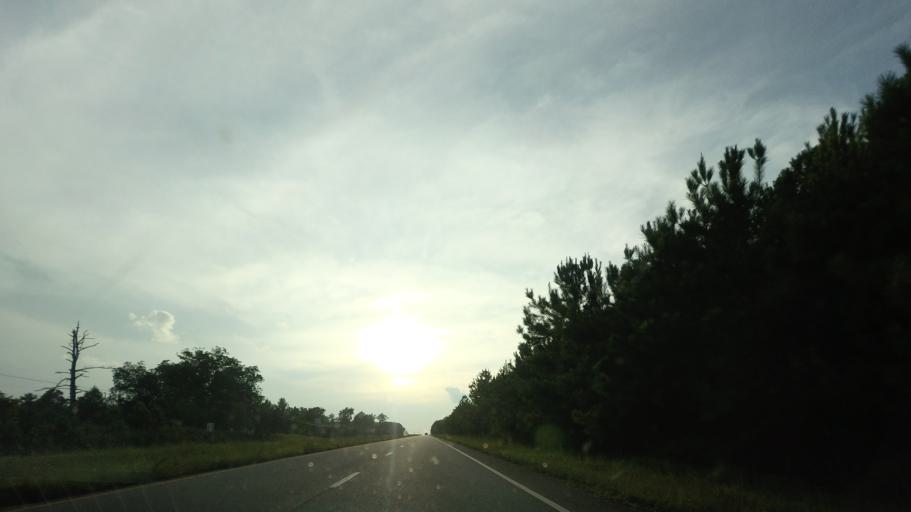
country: US
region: Georgia
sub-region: Wilkinson County
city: Gordon
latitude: 32.8482
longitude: -83.4268
